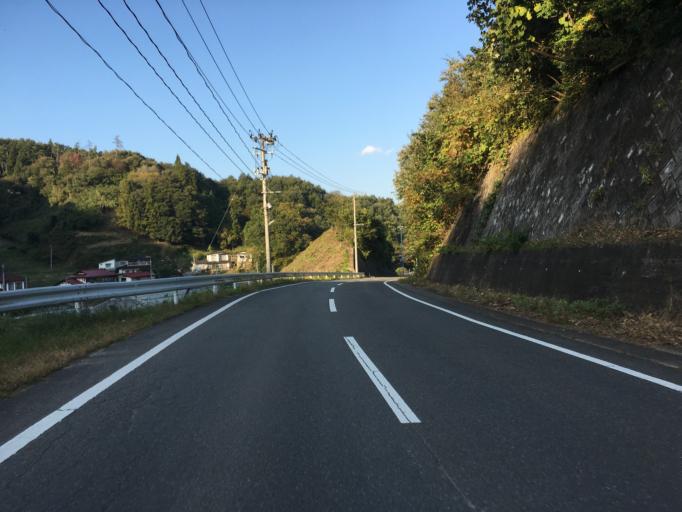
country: JP
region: Fukushima
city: Fukushima-shi
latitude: 37.6544
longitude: 140.5896
